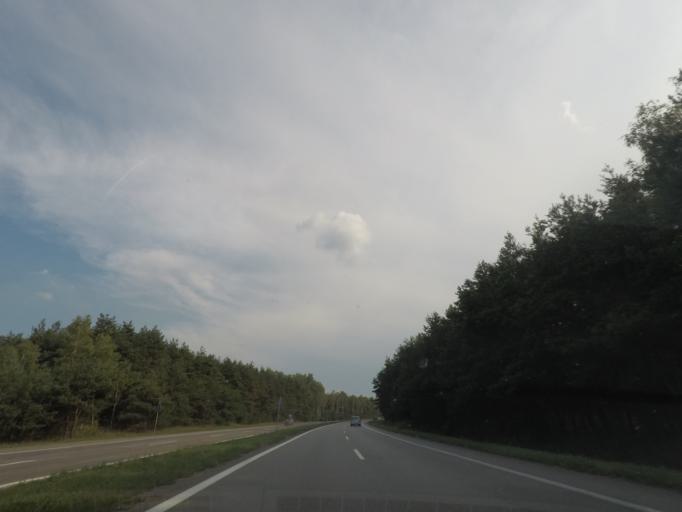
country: PL
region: Silesian Voivodeship
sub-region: Dabrowa Gornicza
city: Dabrowa Gornicza
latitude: 50.3688
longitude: 19.2497
